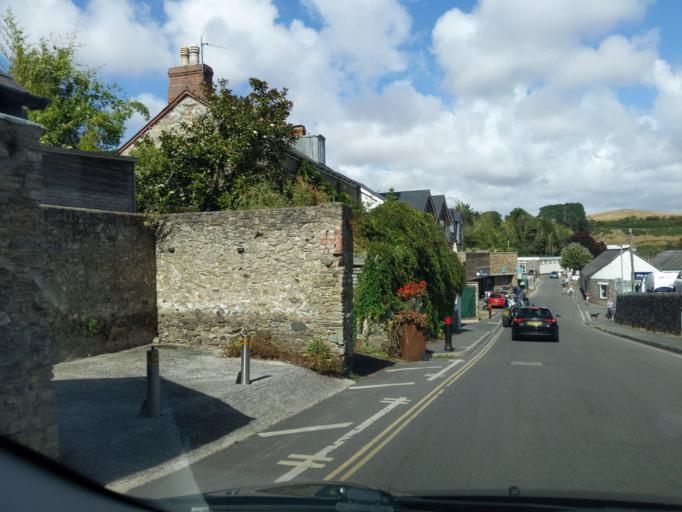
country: GB
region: England
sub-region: Devon
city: Salcombe
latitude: 50.2394
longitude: -3.7708
